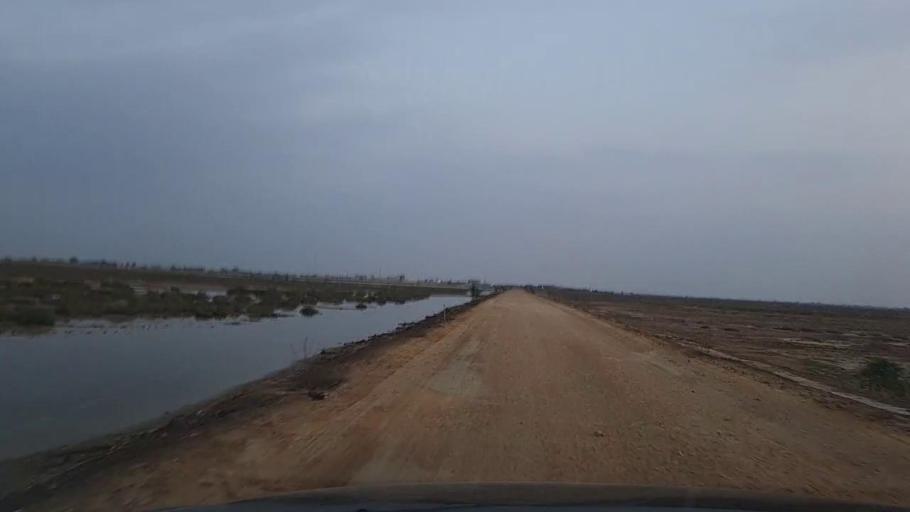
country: PK
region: Sindh
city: Jati
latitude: 24.4959
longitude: 68.3861
